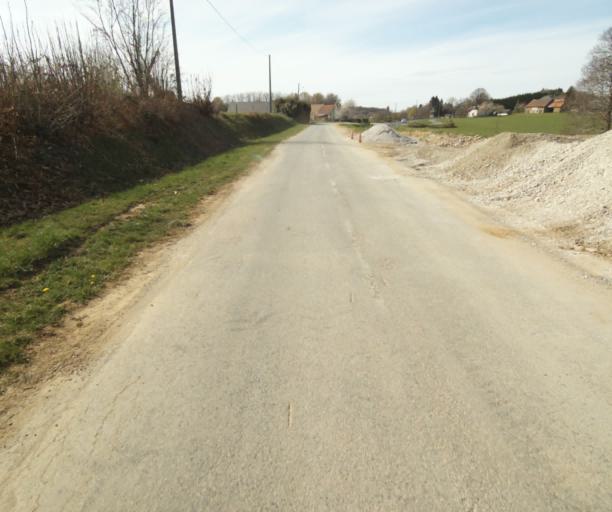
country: FR
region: Limousin
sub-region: Departement de la Correze
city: Seilhac
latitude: 45.3447
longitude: 1.7438
